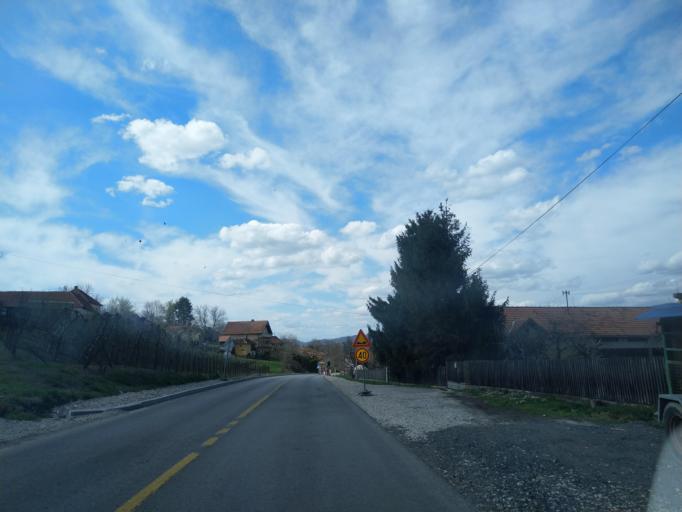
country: RS
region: Central Serbia
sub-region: Zlatiborski Okrug
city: Pozega
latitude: 43.8231
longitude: 20.0825
